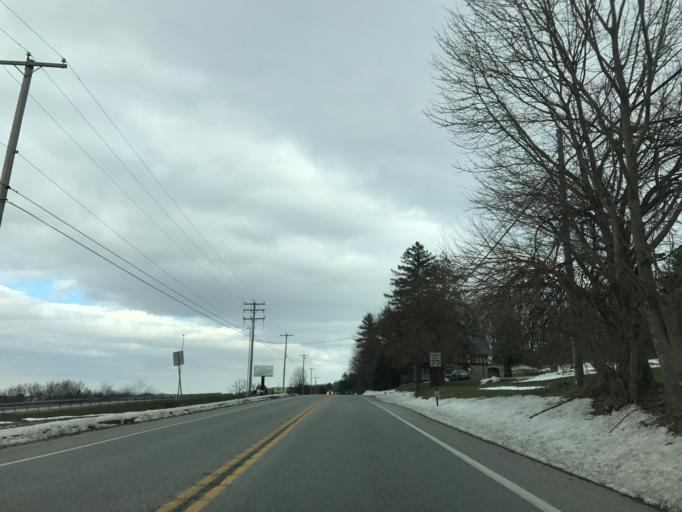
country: US
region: Pennsylvania
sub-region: York County
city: Spring Grove
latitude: 39.8635
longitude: -76.8745
